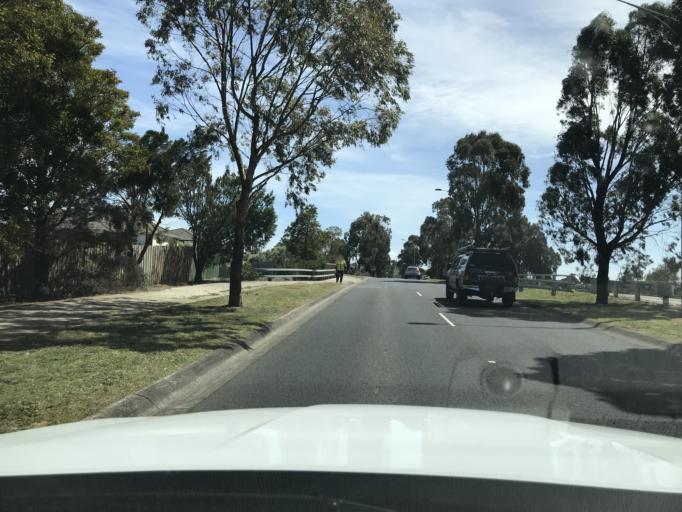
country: AU
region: Victoria
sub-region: Hume
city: Roxburgh Park
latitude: -37.6229
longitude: 144.9326
